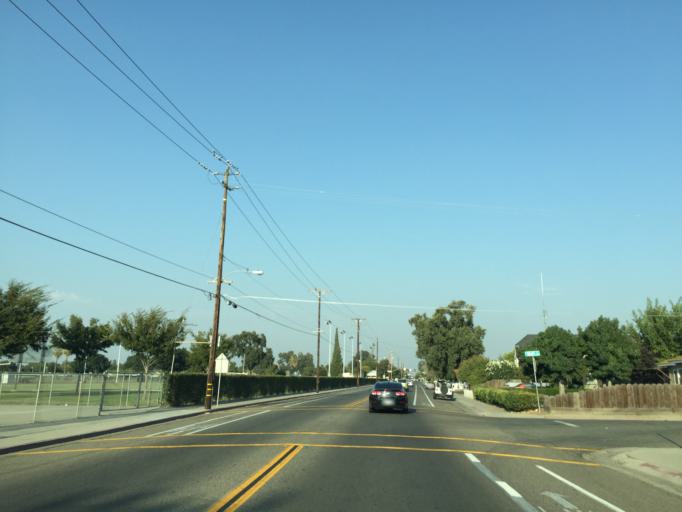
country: US
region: California
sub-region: Tulare County
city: Visalia
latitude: 36.3201
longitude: -119.2996
